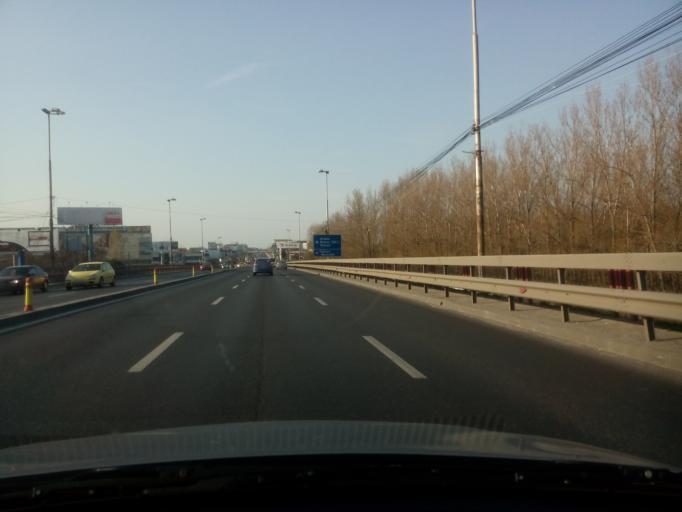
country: RO
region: Ilfov
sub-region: Comuna Otopeni
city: Otopeni
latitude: 44.5355
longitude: 26.0684
